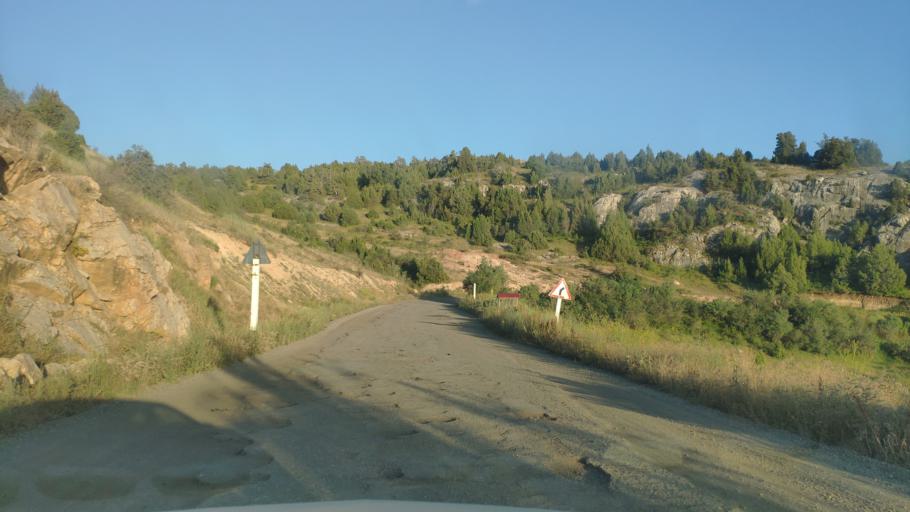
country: TJ
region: Viloyati Sughd
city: Ayni
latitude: 39.6350
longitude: 68.4629
